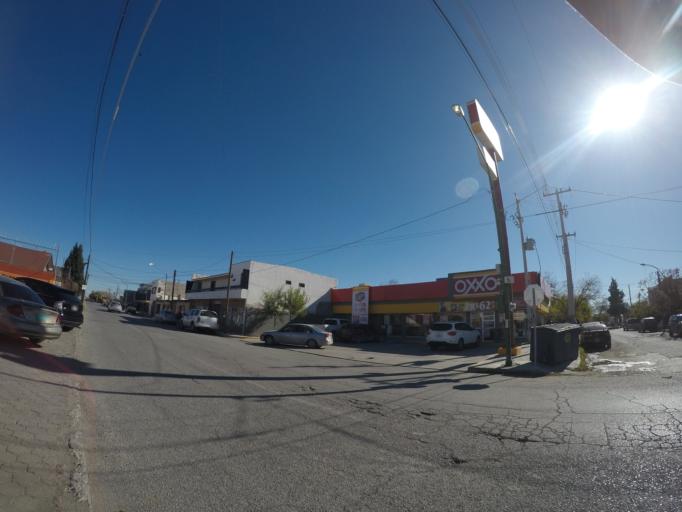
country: MX
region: Chihuahua
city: Ciudad Juarez
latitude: 31.7403
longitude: -106.4610
